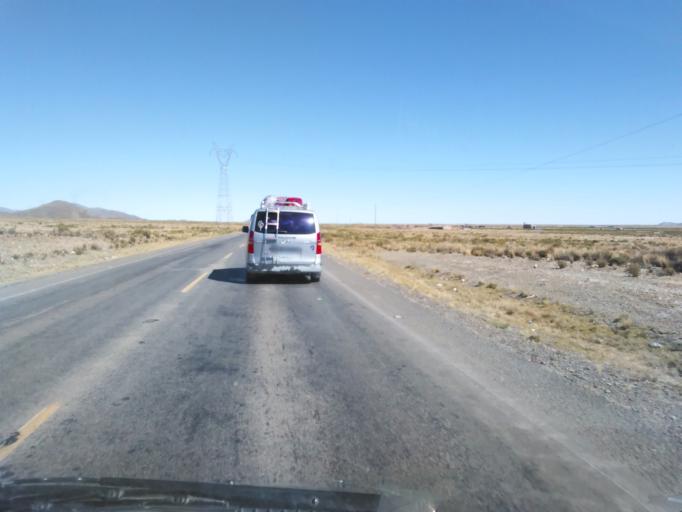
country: BO
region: Oruro
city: Machacamarca
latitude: -18.0758
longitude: -67.0059
